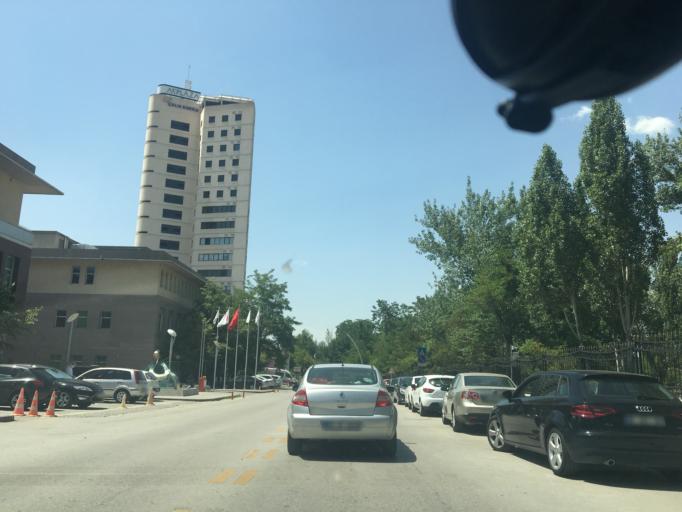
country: TR
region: Ankara
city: Ankara
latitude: 39.9132
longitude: 32.8070
